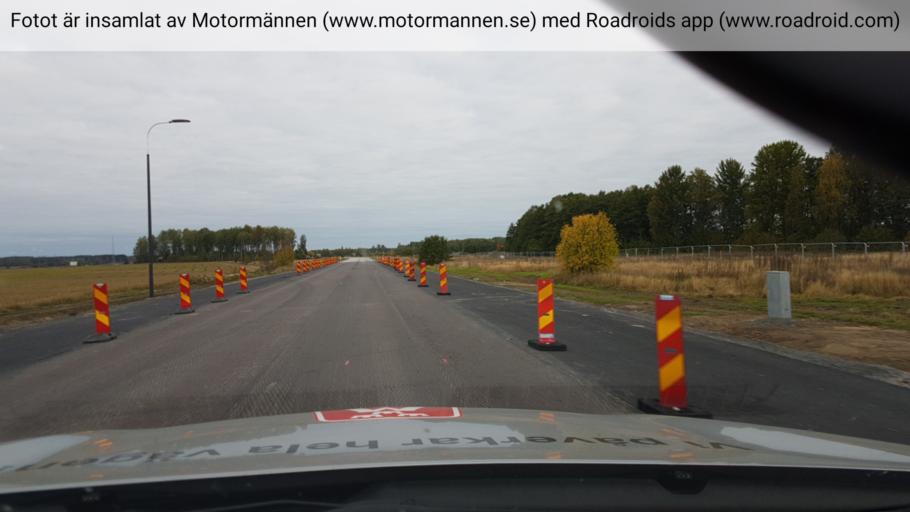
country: SE
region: Uppsala
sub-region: Tierps Kommun
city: Tierp
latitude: 60.3372
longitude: 17.5054
